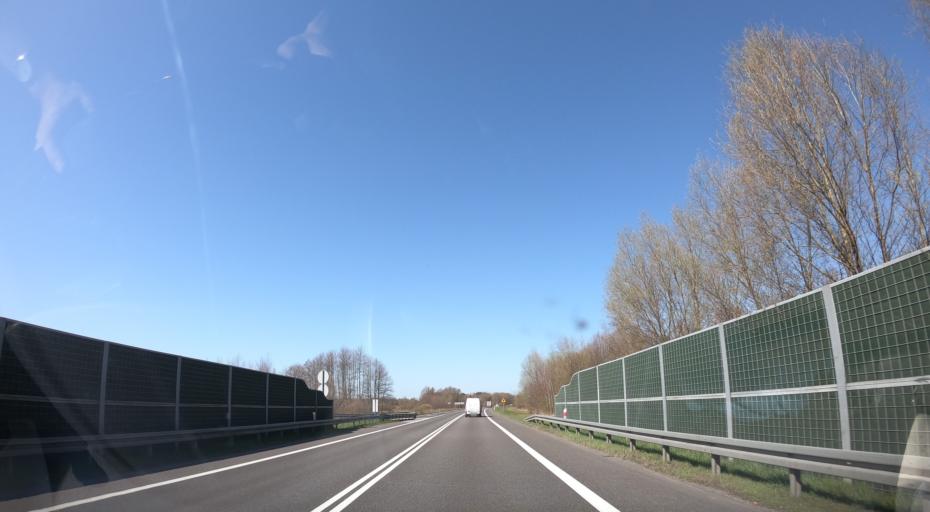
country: PL
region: West Pomeranian Voivodeship
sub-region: Powiat kamienski
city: Wolin
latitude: 53.8444
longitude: 14.7150
